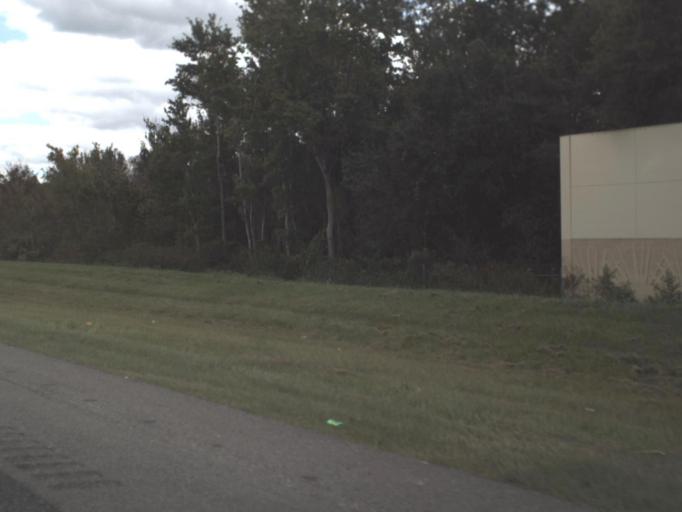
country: US
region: Florida
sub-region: Orange County
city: Winter Garden
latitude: 28.5450
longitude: -81.6017
